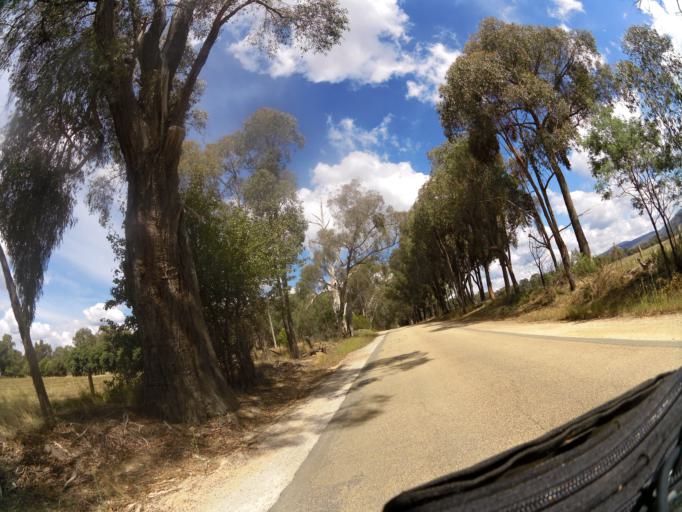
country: AU
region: Victoria
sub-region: Benalla
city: Benalla
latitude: -36.7734
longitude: 145.9745
